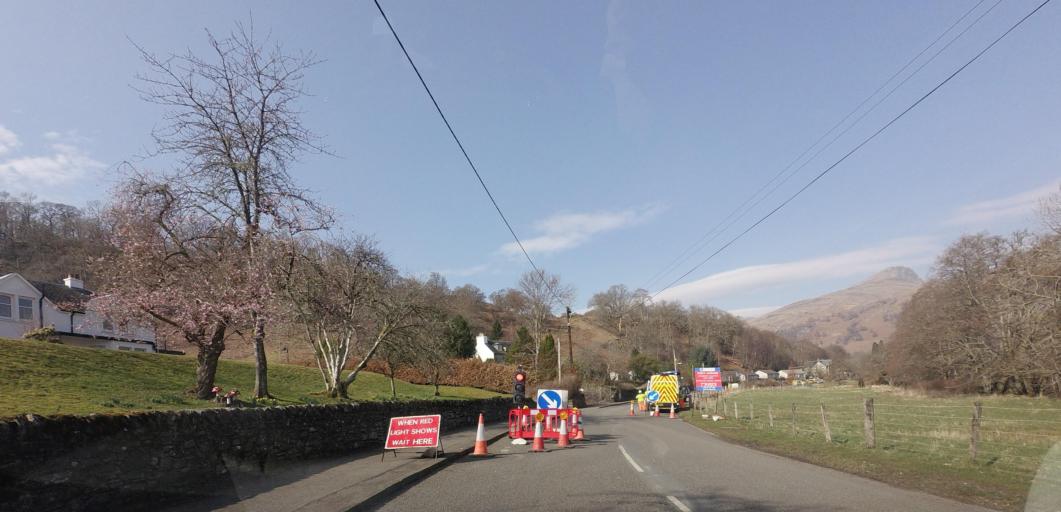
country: GB
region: Scotland
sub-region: Stirling
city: Callander
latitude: 56.4701
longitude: -4.3197
